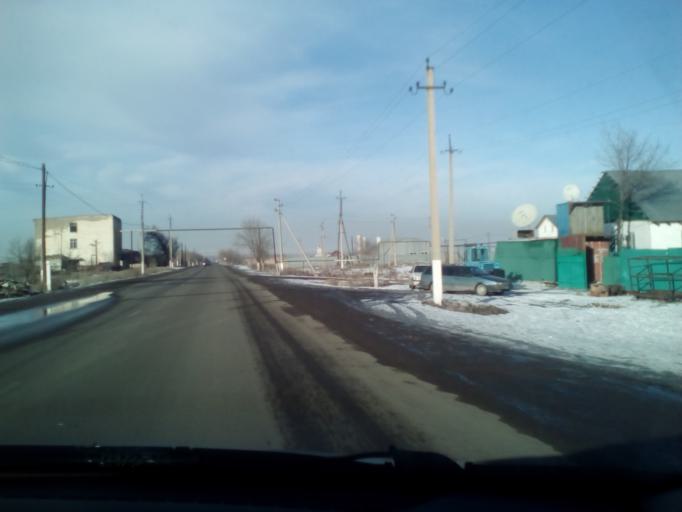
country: KZ
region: Almaty Oblysy
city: Burunday
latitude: 43.1910
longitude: 76.4148
